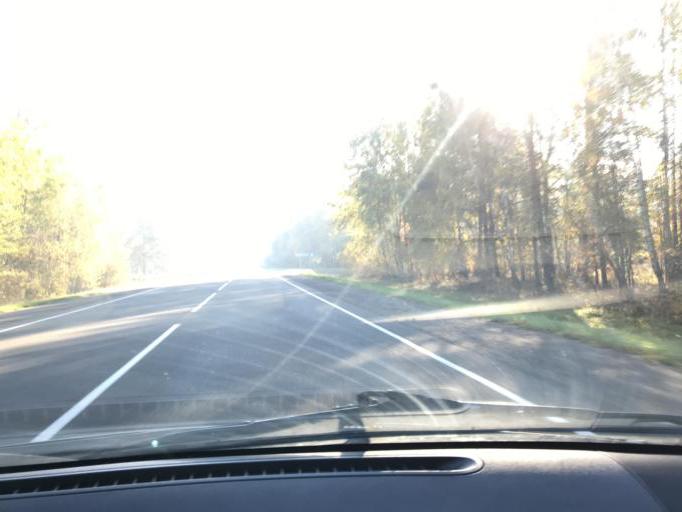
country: BY
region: Brest
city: Horad Luninyets
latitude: 52.2971
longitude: 26.7403
